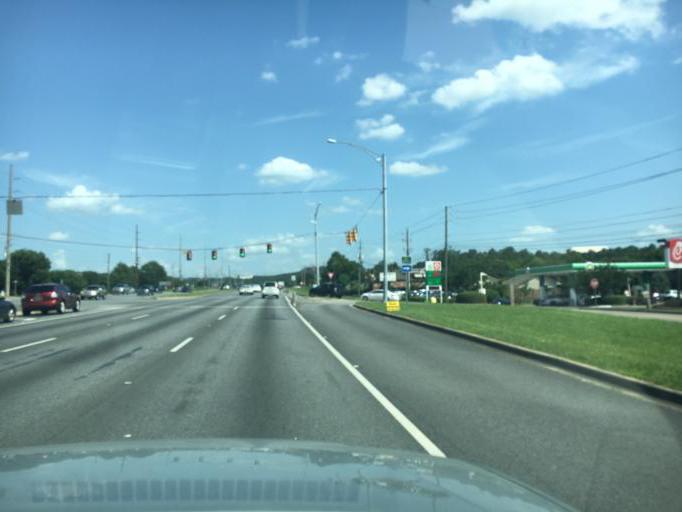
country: US
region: Alabama
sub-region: Shelby County
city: Lake Purdy
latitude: 33.4285
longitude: -86.7081
